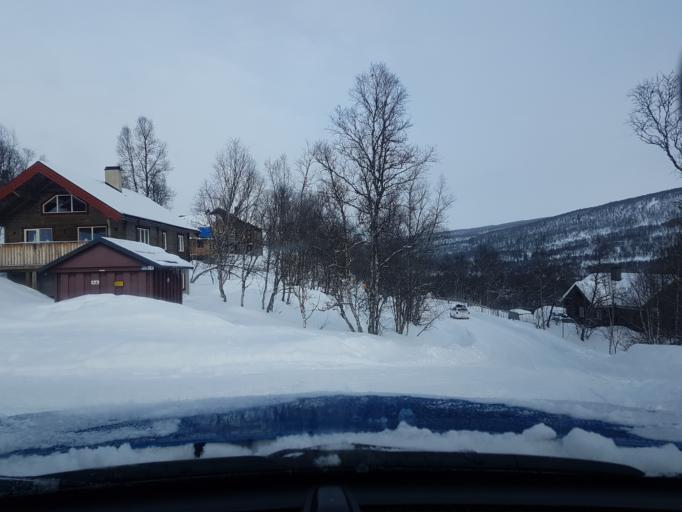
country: NO
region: Sor-Trondelag
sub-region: Tydal
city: Aas
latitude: 62.6917
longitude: 12.3990
